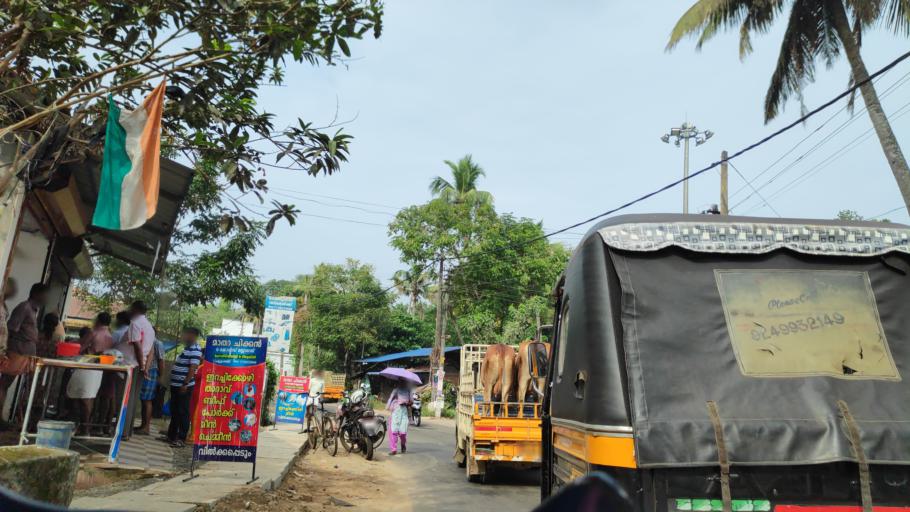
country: IN
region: Kerala
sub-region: Alappuzha
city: Kutiatodu
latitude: 9.7947
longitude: 76.3565
